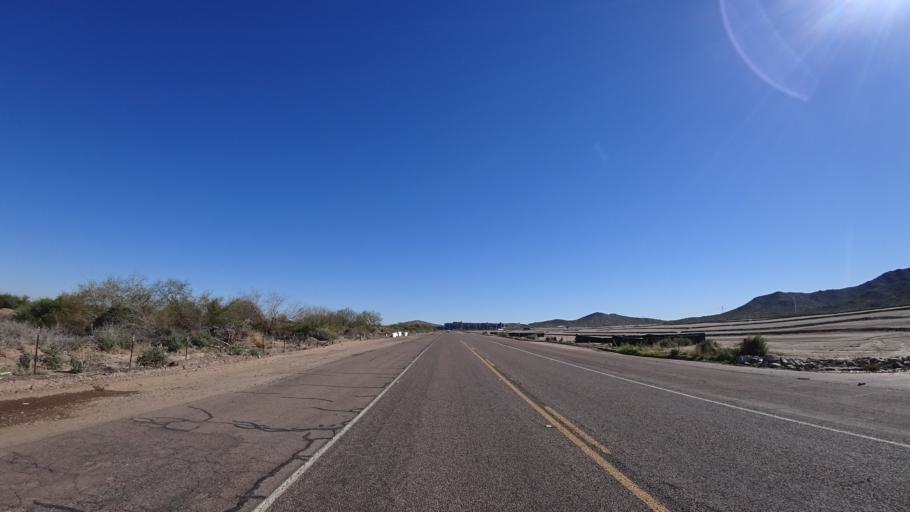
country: US
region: Arizona
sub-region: Maricopa County
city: Avondale
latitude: 33.3756
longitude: -112.3318
